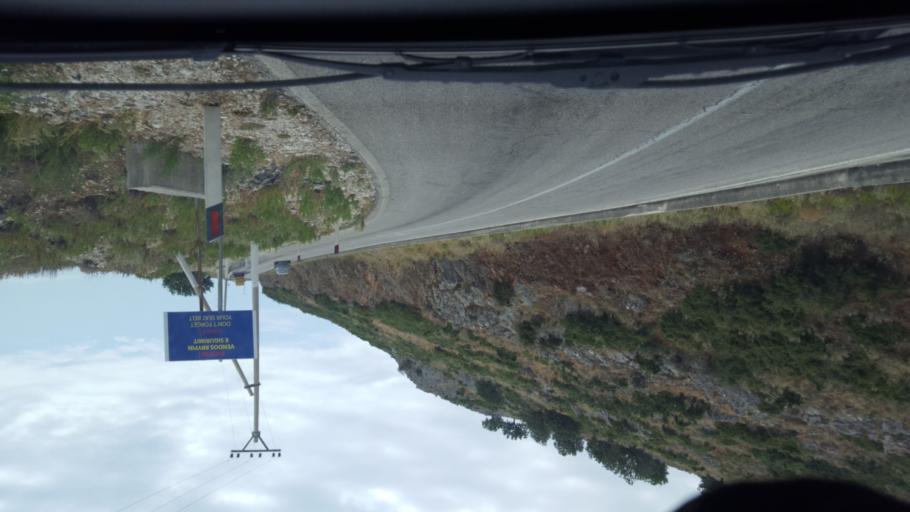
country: AL
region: Vlore
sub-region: Rrethi i Sarandes
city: Lukove
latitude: 40.0466
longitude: 19.8712
